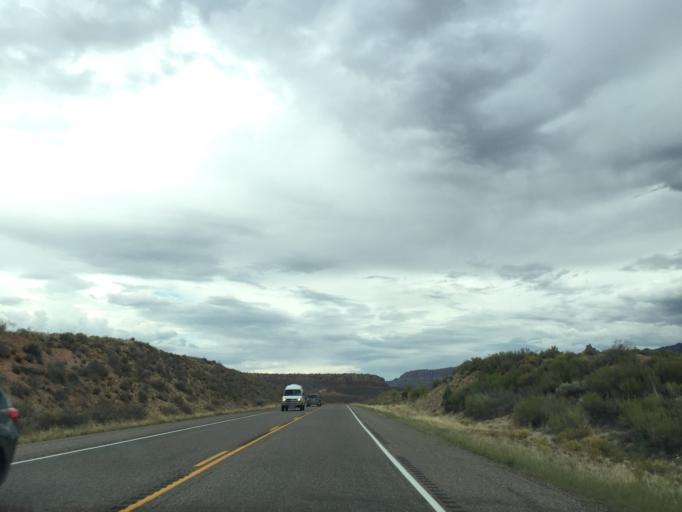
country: US
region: Utah
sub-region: Washington County
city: LaVerkin
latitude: 37.1718
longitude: -113.0885
